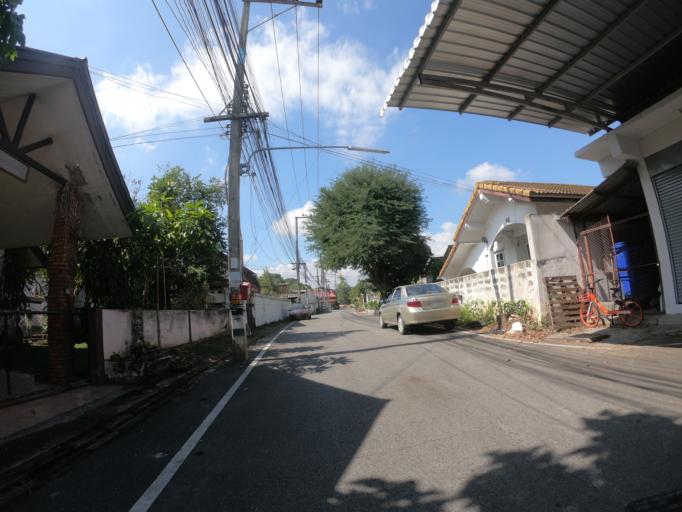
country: TH
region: Chiang Mai
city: Chiang Mai
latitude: 18.7433
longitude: 98.9561
